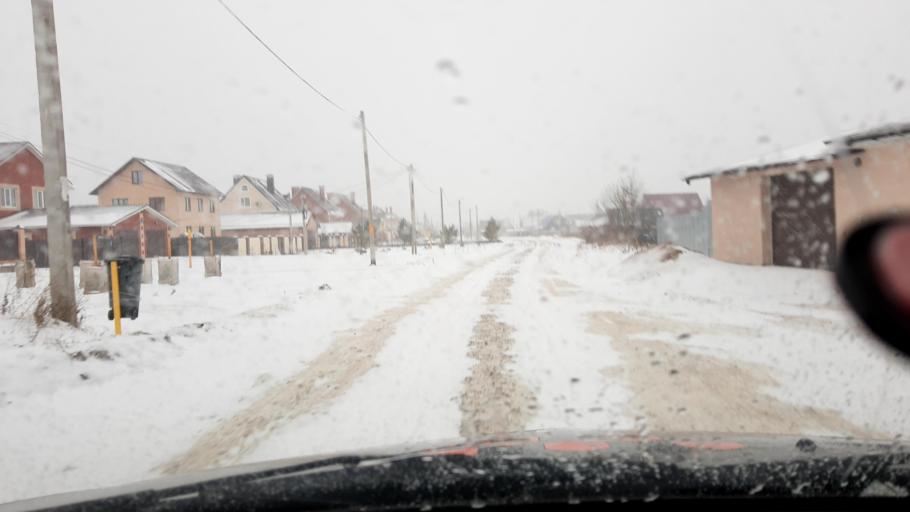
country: RU
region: Bashkortostan
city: Ufa
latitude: 54.5492
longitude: 55.9476
